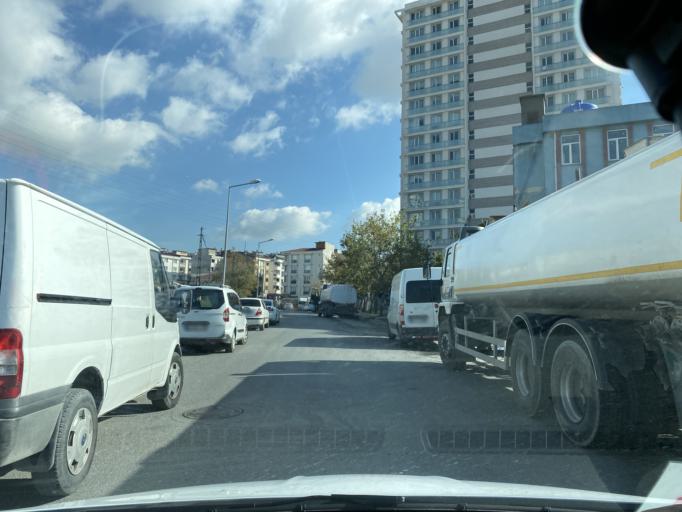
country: TR
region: Istanbul
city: Esenyurt
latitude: 41.0278
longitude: 28.6695
